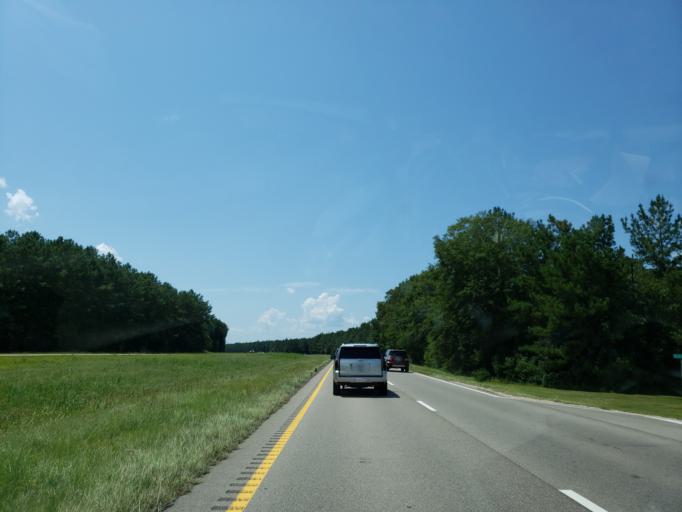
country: US
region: Mississippi
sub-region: Forrest County
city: Hattiesburg
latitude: 31.2373
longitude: -89.2117
